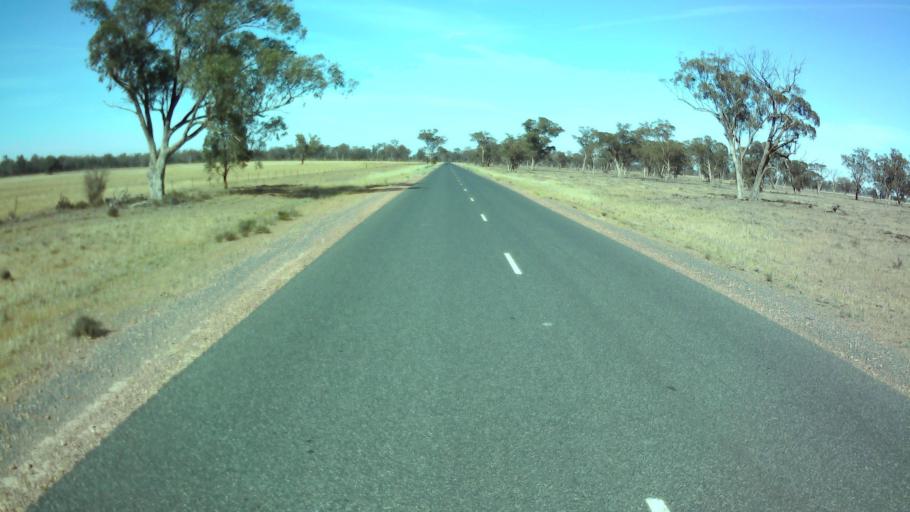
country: AU
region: New South Wales
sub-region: Weddin
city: Grenfell
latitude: -34.1079
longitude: 147.8589
